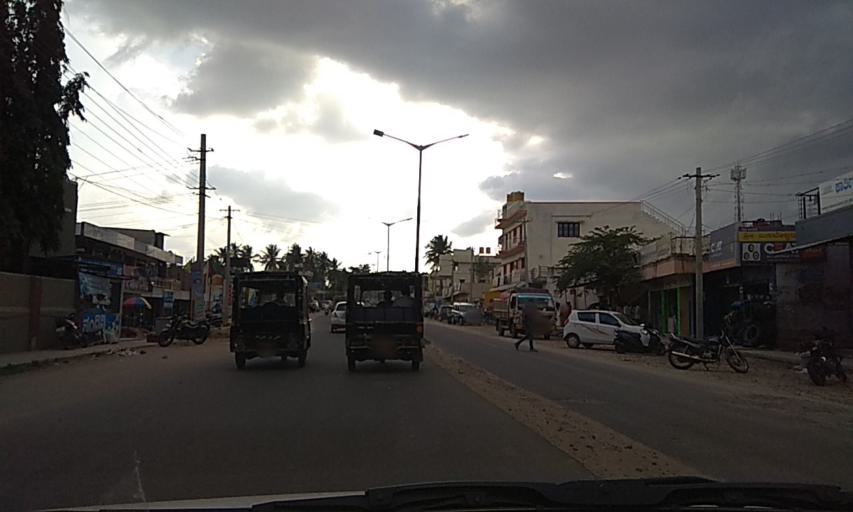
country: IN
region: Karnataka
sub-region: Chamrajnagar
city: Gundlupet
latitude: 11.8064
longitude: 76.6906
